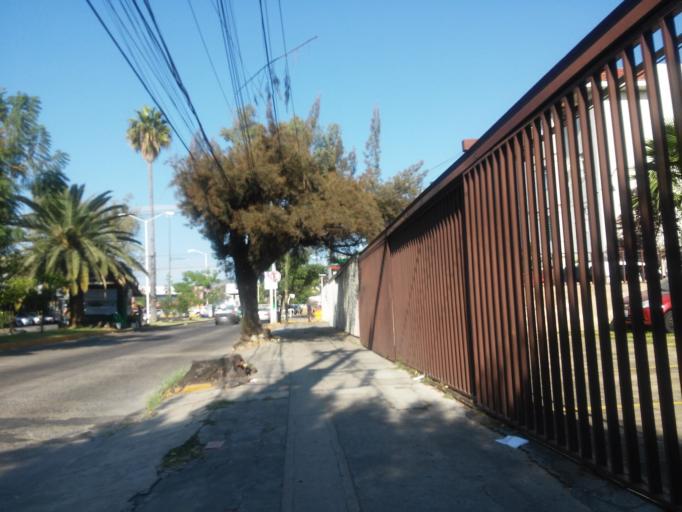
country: MX
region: Jalisco
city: Guadalajara
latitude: 20.6342
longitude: -103.4124
